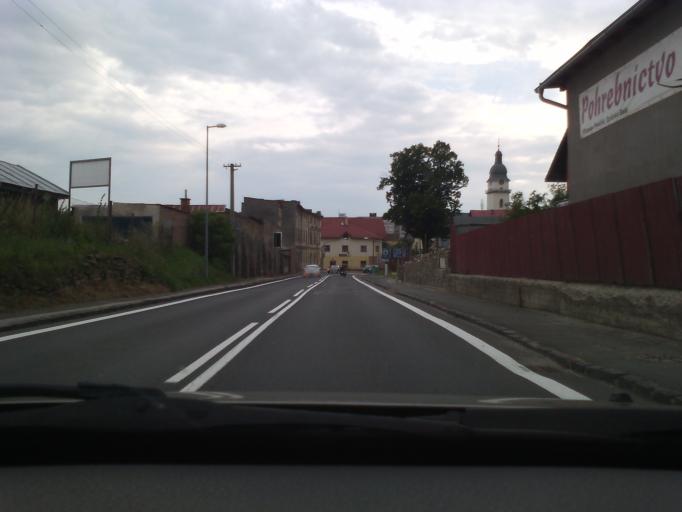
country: SK
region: Presovsky
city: Spisska Bela
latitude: 49.1898
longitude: 20.4600
